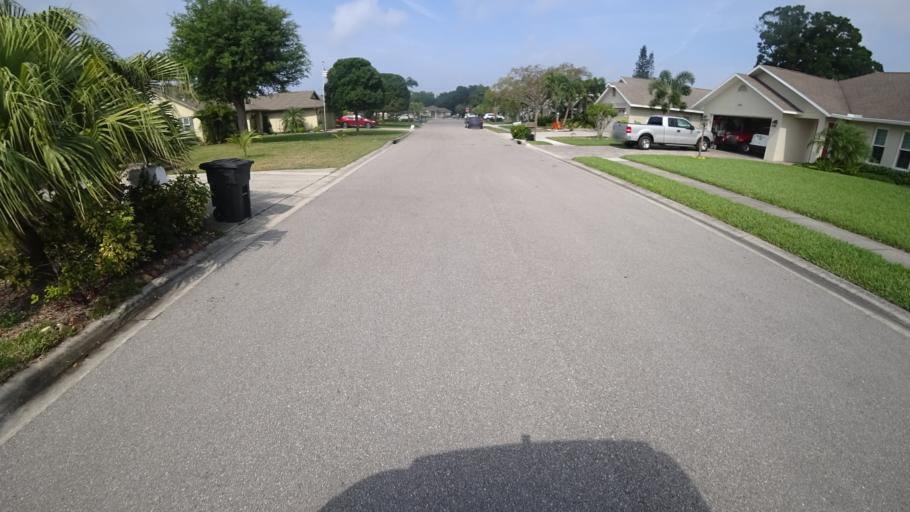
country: US
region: Florida
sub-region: Manatee County
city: West Bradenton
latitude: 27.4827
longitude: -82.6142
